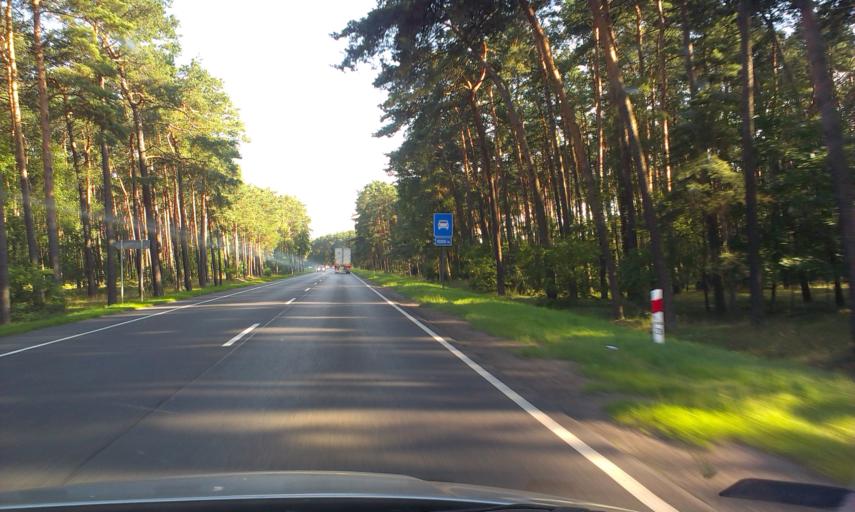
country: PL
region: Kujawsko-Pomorskie
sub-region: Powiat bydgoski
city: Biale Blota
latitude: 53.1119
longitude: 17.8840
